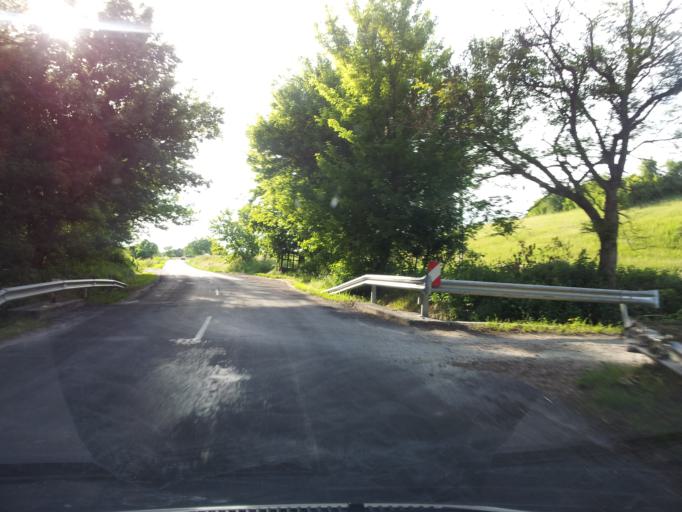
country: HU
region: Komarom-Esztergom
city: Esztergom
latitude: 47.7563
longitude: 18.7751
